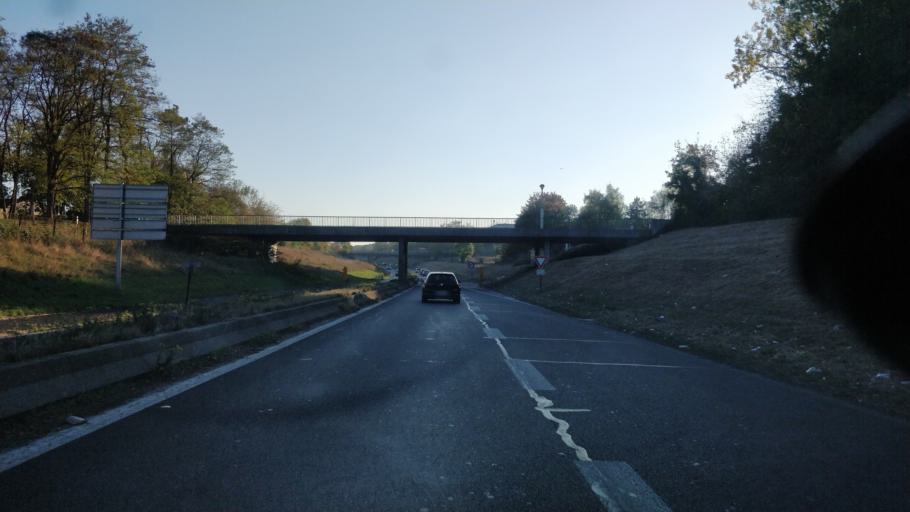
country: FR
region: Ile-de-France
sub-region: Departement de Seine-et-Marne
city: Noisiel
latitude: 48.8439
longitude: 2.6293
